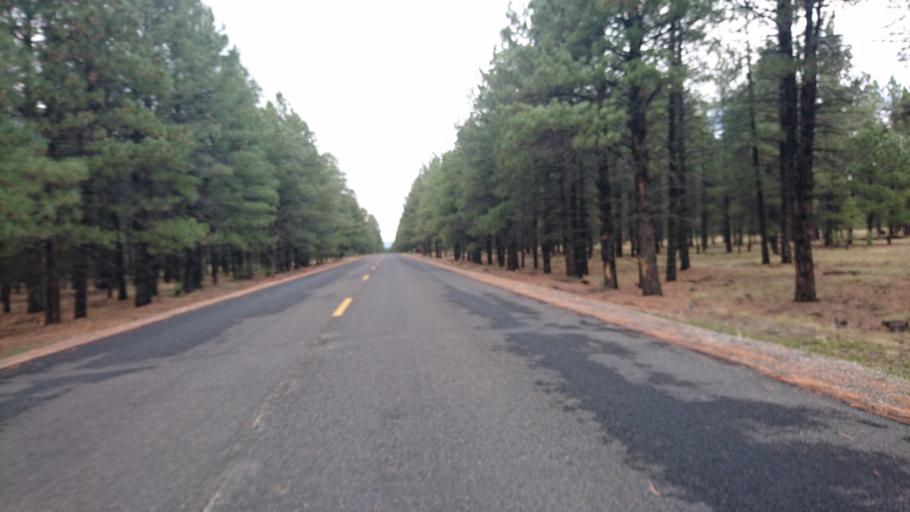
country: US
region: Arizona
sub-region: Coconino County
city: Parks
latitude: 35.2556
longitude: -111.8644
